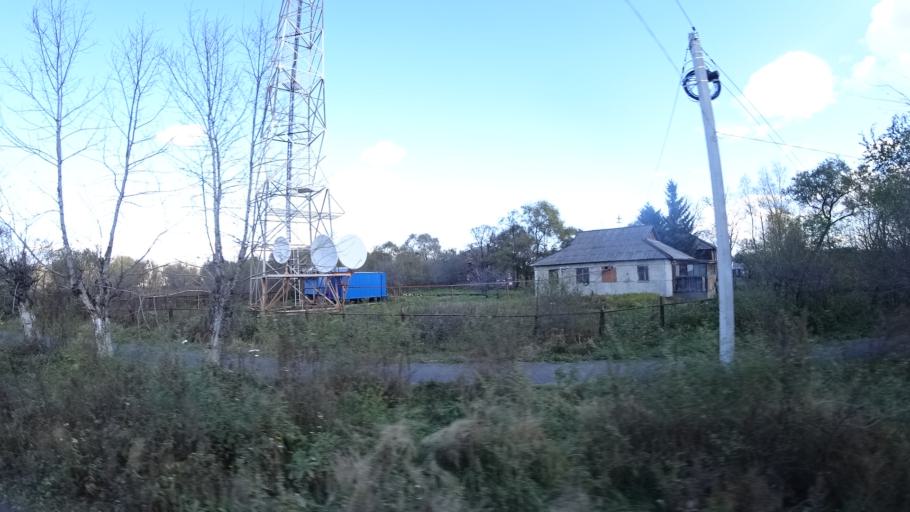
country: RU
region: Khabarovsk Krai
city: Amursk
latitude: 50.0958
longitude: 136.4976
